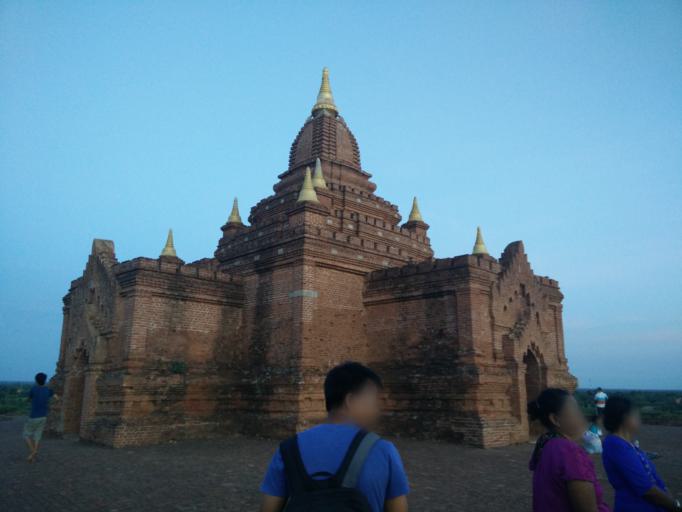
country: MM
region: Magway
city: Pakokku
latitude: 21.1585
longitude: 94.8891
